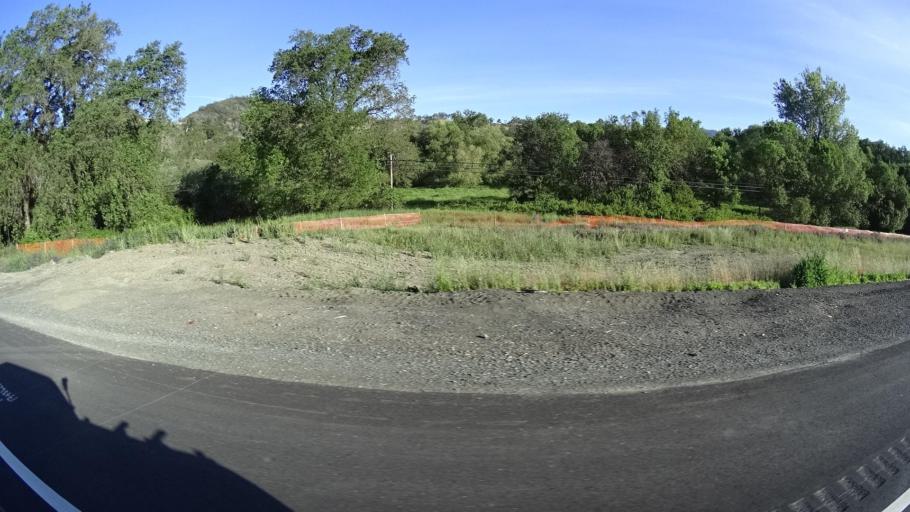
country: US
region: California
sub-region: Lake County
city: Upper Lake
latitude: 39.1667
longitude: -122.9629
